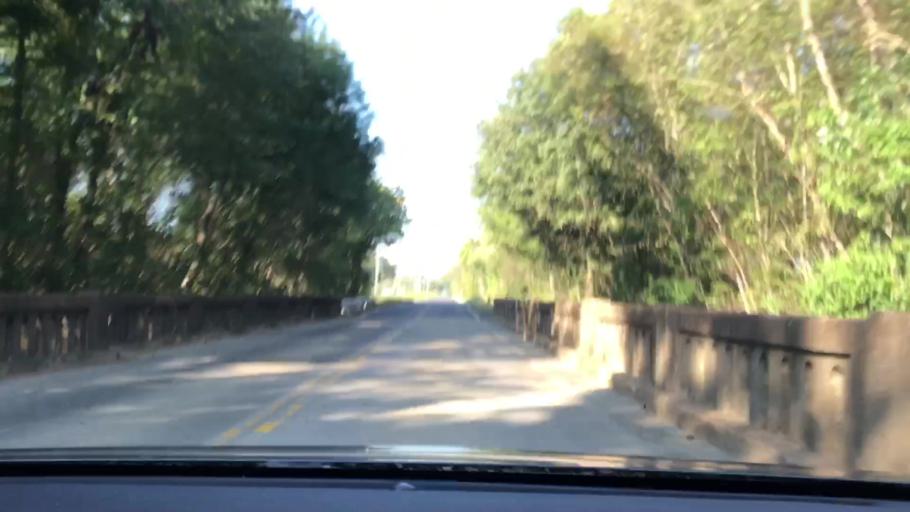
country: US
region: Kentucky
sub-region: Marshall County
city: Benton
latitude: 36.7688
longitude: -88.2823
